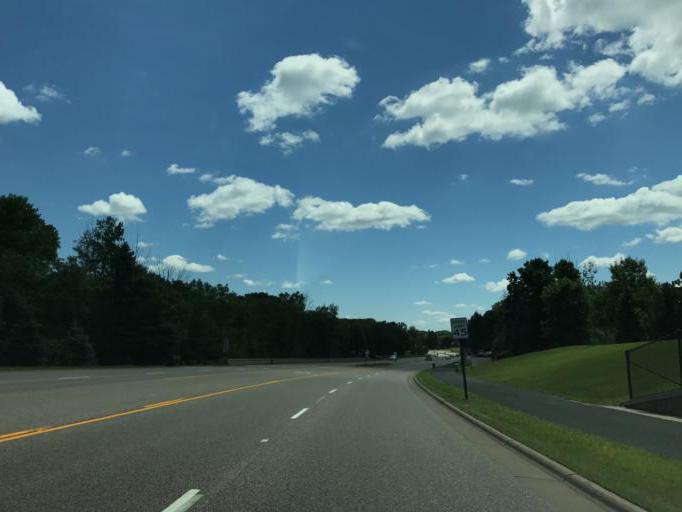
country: US
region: Minnesota
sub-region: Hennepin County
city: Maple Grove
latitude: 45.0787
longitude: -93.4731
